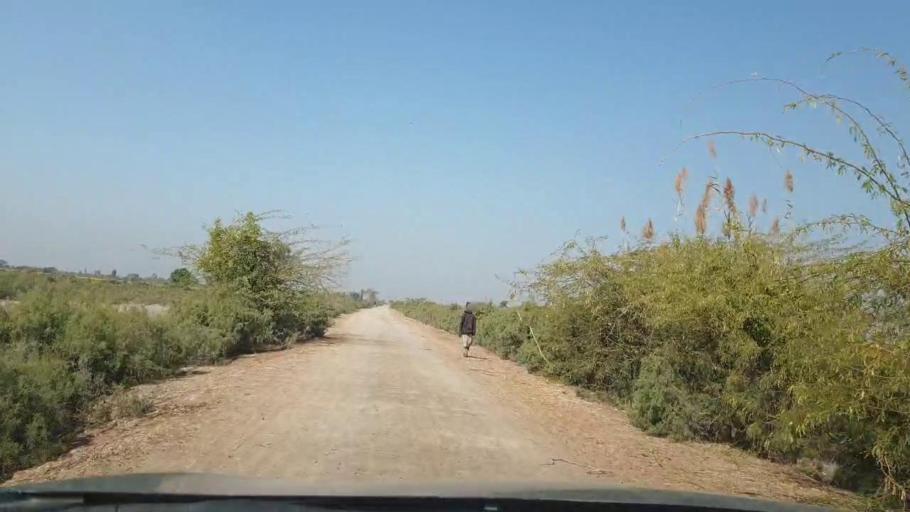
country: PK
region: Sindh
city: Berani
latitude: 25.6796
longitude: 68.8961
